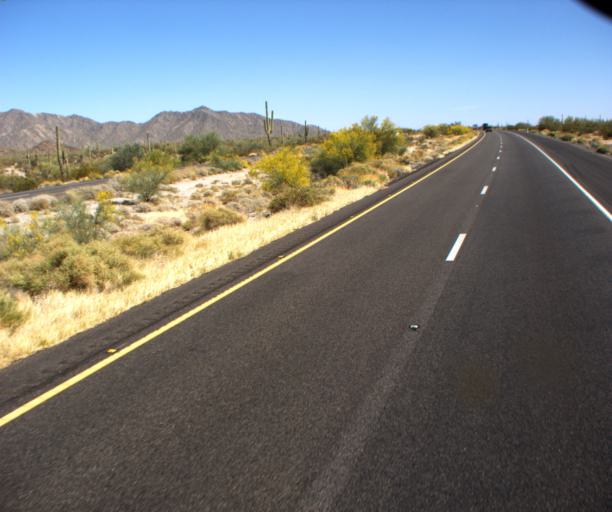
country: US
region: Arizona
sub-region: Maricopa County
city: Gila Bend
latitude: 32.8743
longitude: -112.4446
